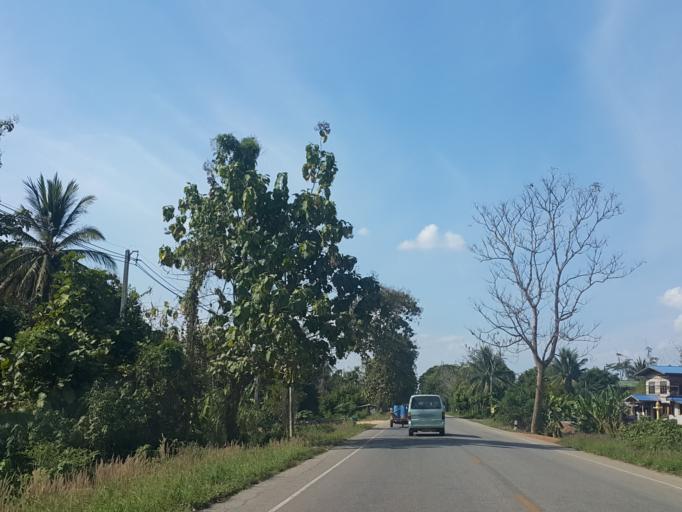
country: TH
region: Sukhothai
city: Sawankhalok
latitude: 17.2554
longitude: 99.8408
